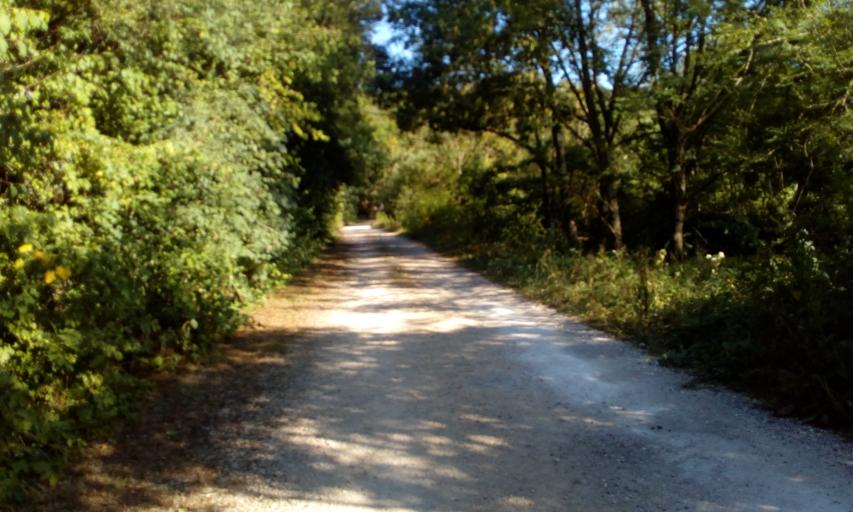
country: FR
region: Lorraine
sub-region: Departement de Meurthe-et-Moselle
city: Pagny-sur-Moselle
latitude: 48.9666
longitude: 5.8875
